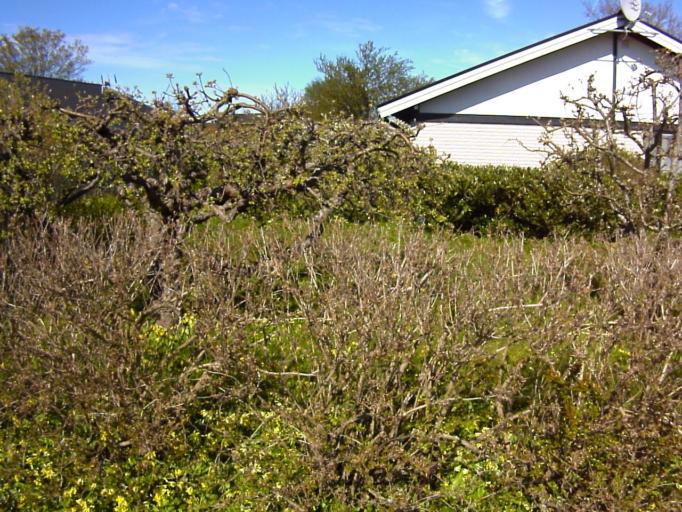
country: SE
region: Skane
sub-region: Kristianstads Kommun
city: Kristianstad
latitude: 56.0091
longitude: 14.1457
